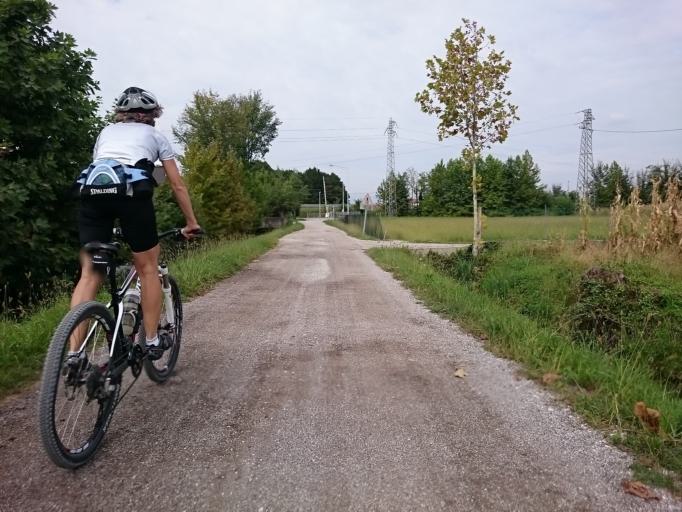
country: IT
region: Veneto
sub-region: Provincia di Padova
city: San Pietro in Gu
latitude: 45.5985
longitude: 11.6593
